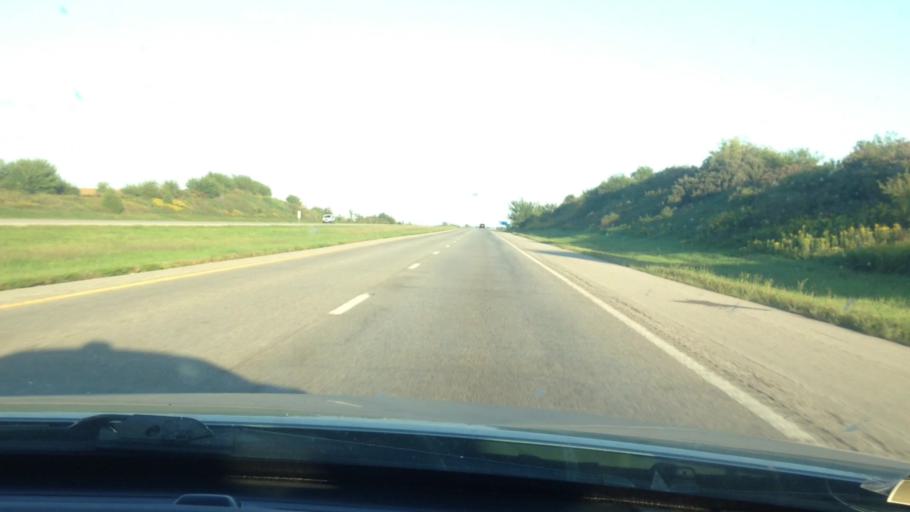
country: US
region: Missouri
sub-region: Platte County
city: Weatherby Lake
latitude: 39.3172
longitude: -94.6873
